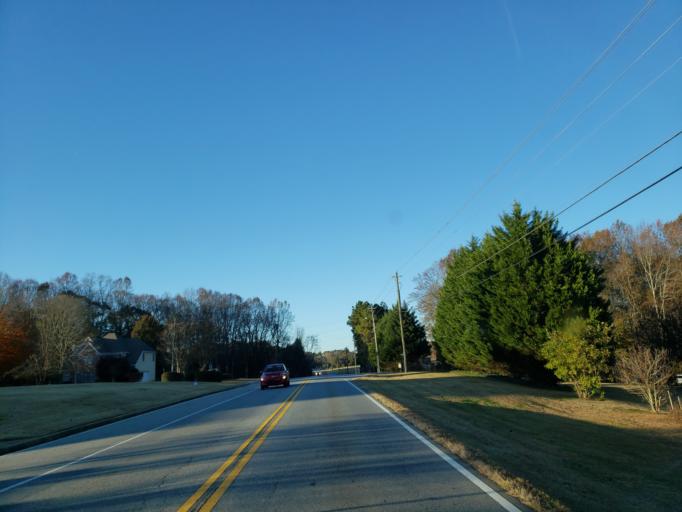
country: US
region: Georgia
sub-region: Cherokee County
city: Holly Springs
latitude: 34.1817
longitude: -84.4203
